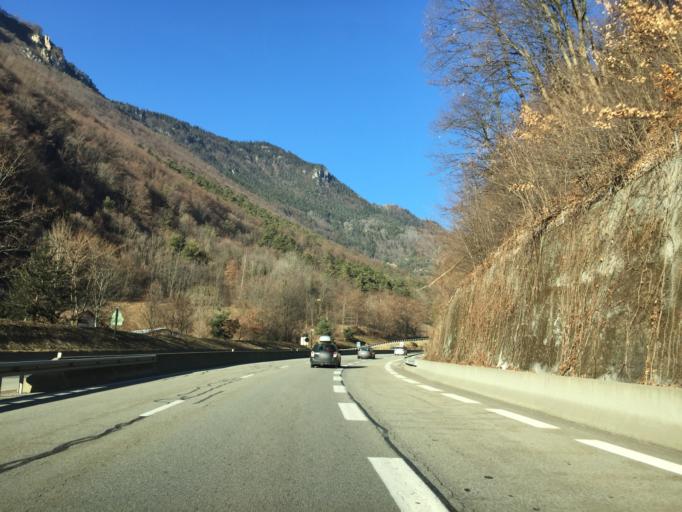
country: FR
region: Rhone-Alpes
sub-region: Departement de la Savoie
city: Moutiers
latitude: 45.5103
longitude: 6.5651
